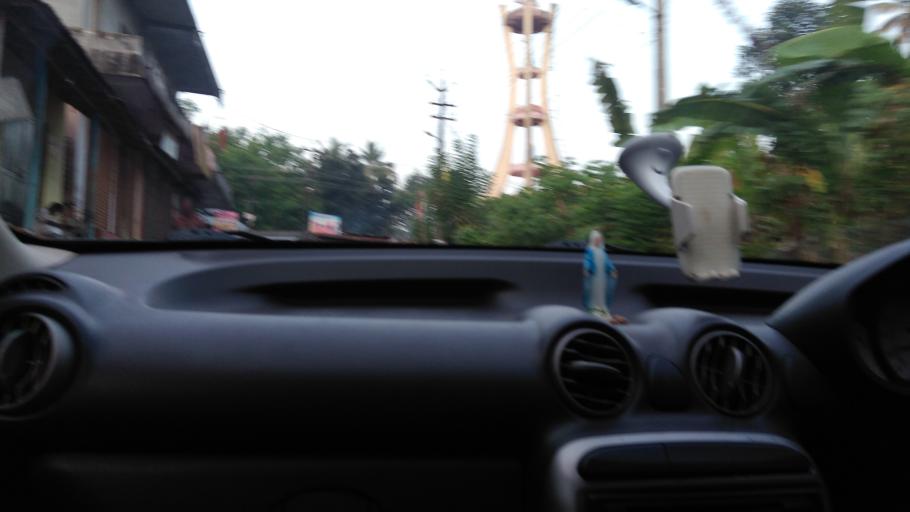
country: IN
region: Kerala
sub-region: Kottayam
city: Palackattumala
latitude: 9.8463
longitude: 76.6505
